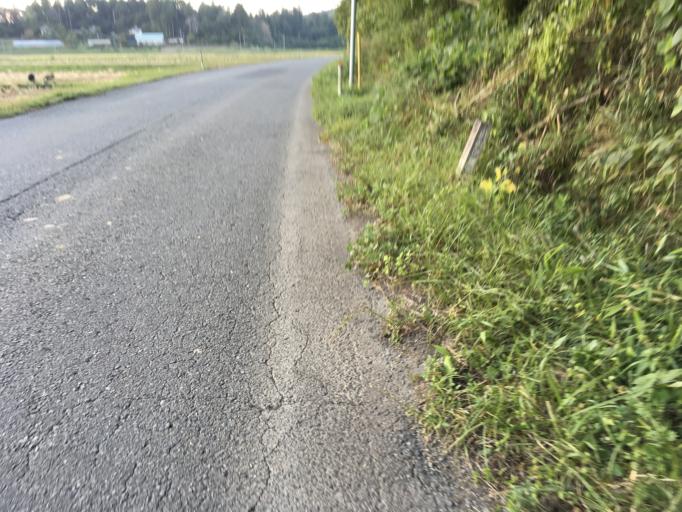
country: JP
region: Iwate
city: Ichinoseki
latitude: 38.7835
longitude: 141.2416
